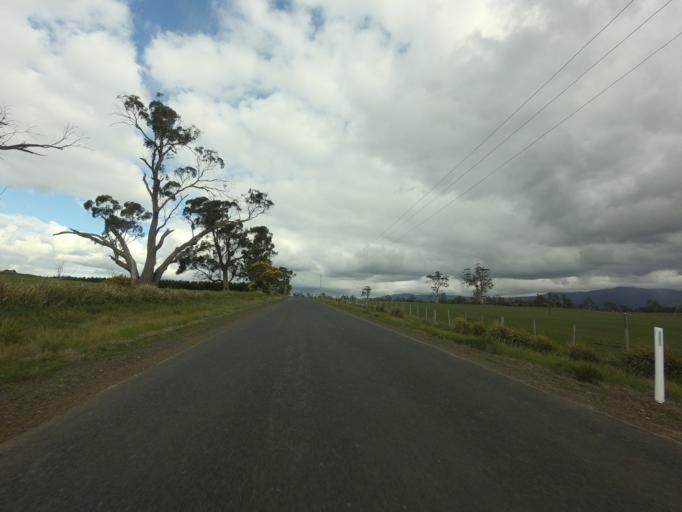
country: AU
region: Tasmania
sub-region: Northern Midlands
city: Longford
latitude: -41.7611
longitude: 147.0829
